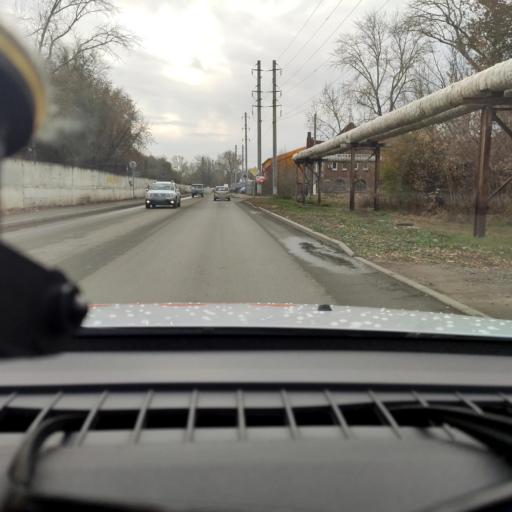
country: RU
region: Samara
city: Chapayevsk
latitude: 52.9721
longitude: 49.7040
